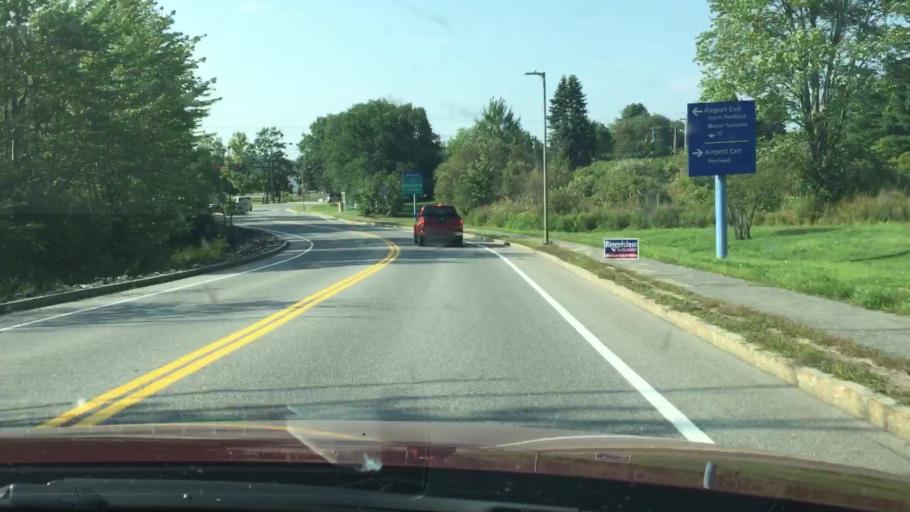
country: US
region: Maine
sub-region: Cumberland County
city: South Portland Gardens
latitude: 43.6519
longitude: -70.3175
